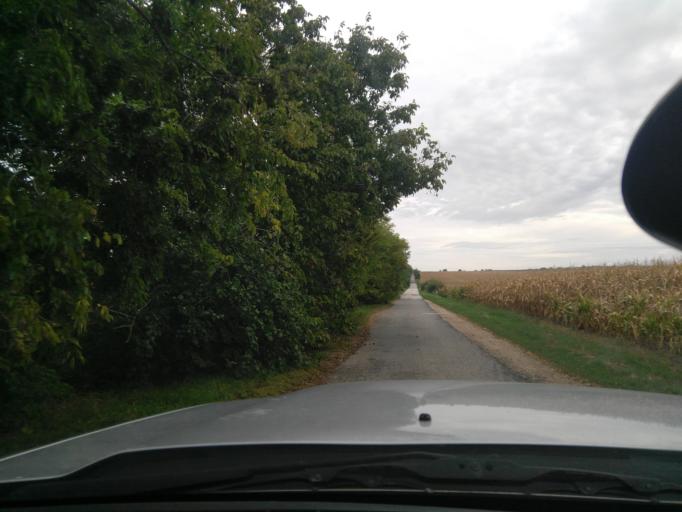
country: HU
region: Fejer
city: Martonvasar
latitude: 47.3535
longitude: 18.7746
